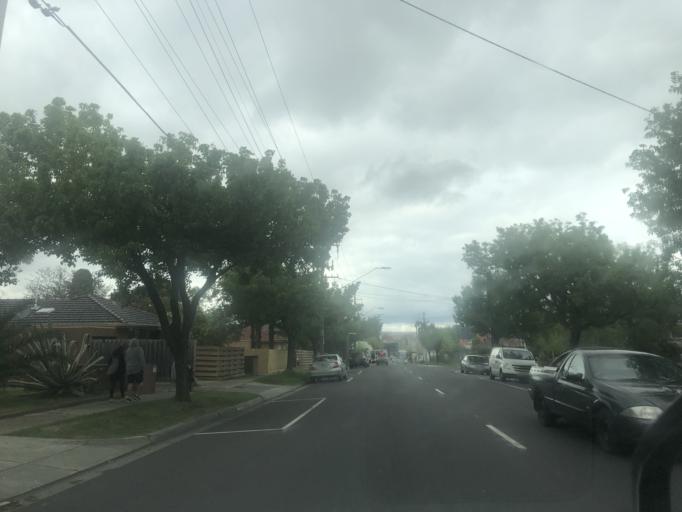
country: AU
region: Victoria
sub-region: Greater Dandenong
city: Dandenong
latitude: -37.9816
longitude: 145.2152
